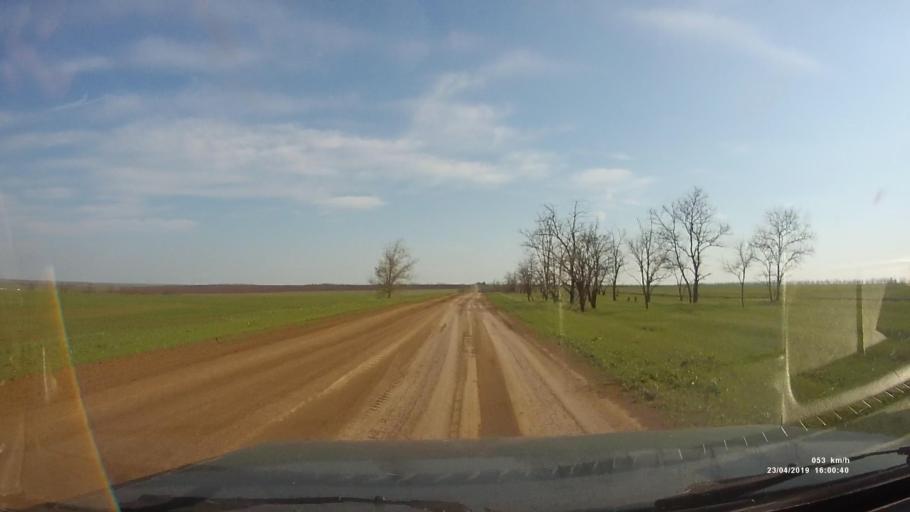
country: RU
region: Rostov
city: Remontnoye
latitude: 46.5075
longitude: 43.1070
